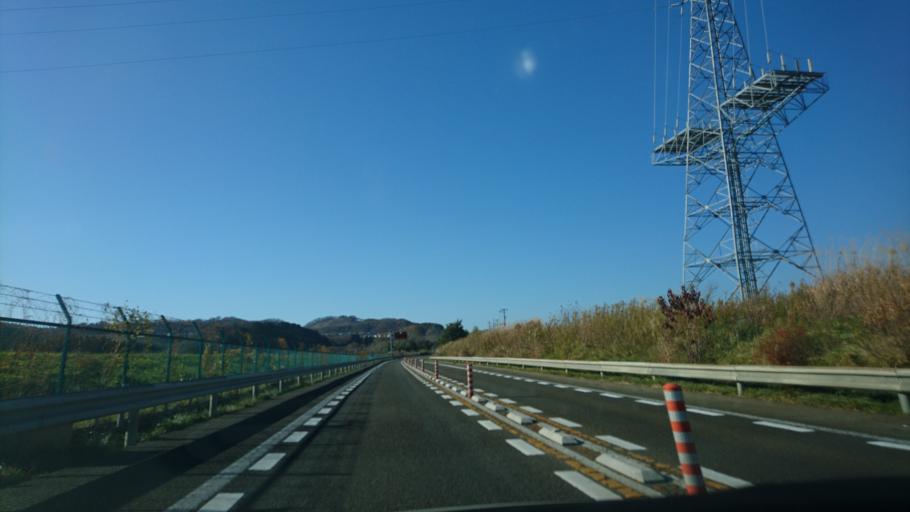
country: JP
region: Miyagi
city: Sendai
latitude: 38.2066
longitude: 140.8509
